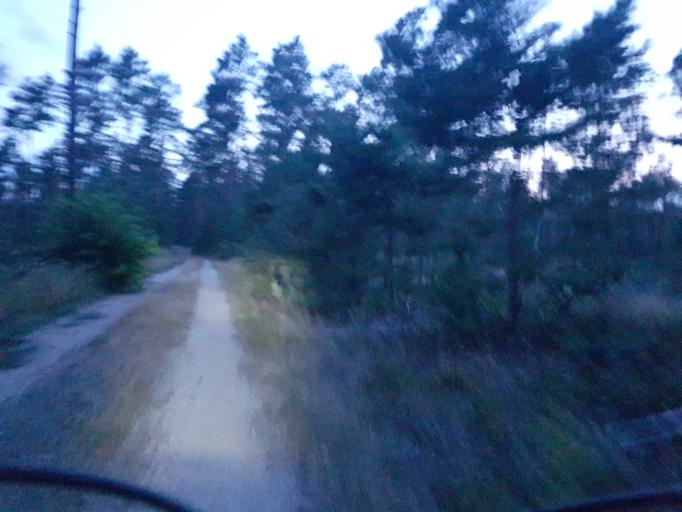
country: DE
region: Brandenburg
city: Trobitz
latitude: 51.5602
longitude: 13.4516
